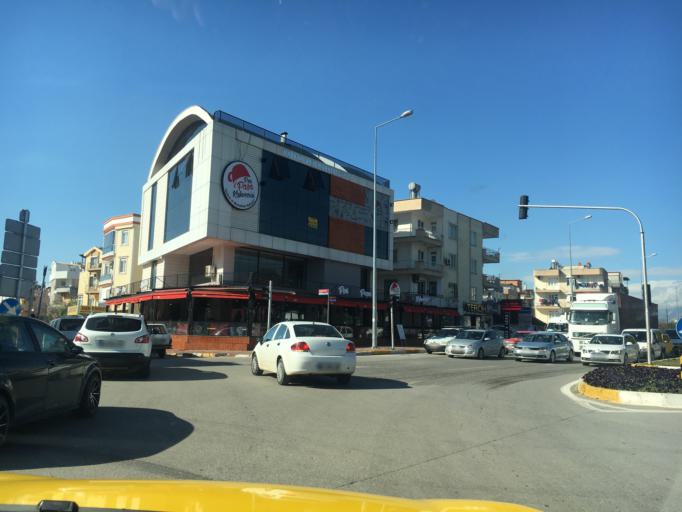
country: TR
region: Antalya
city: Antalya
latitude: 36.9189
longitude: 30.7084
